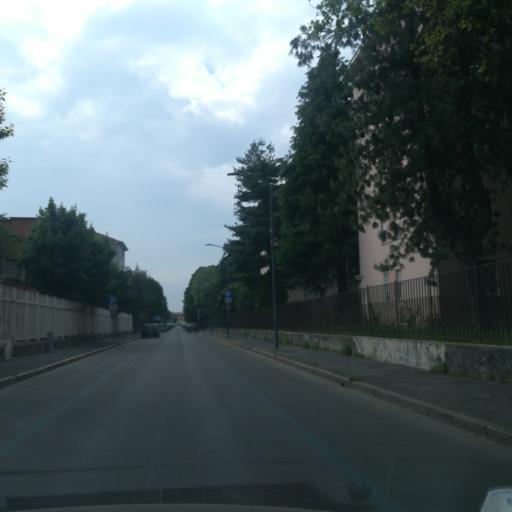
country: IT
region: Lombardy
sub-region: Citta metropolitana di Milano
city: Bresso
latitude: 45.5045
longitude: 9.1964
